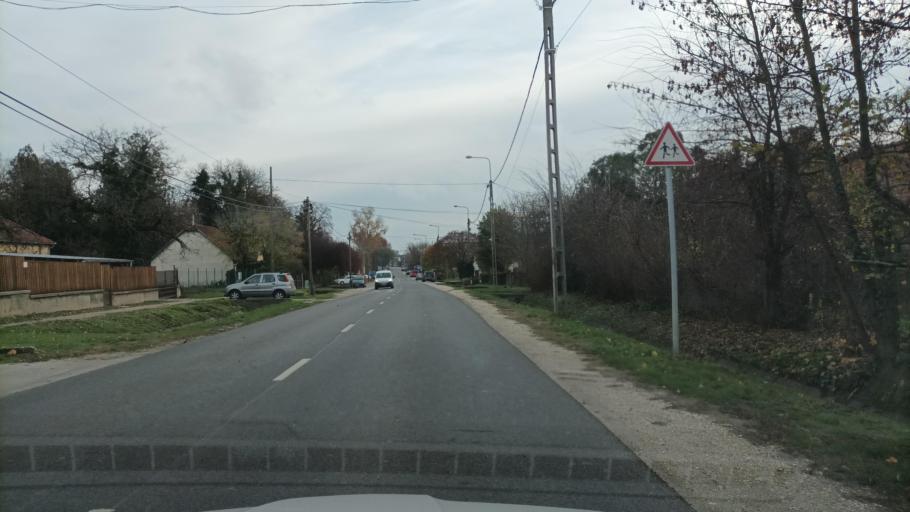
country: HU
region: Pest
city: Ocsa
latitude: 47.2974
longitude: 19.2227
